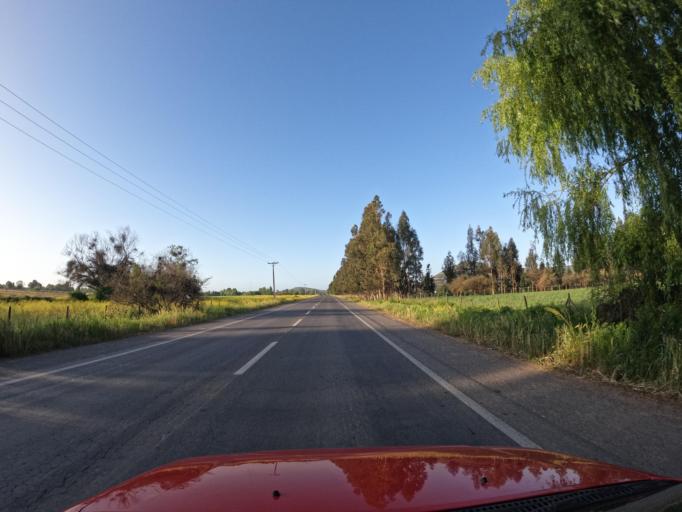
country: CL
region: O'Higgins
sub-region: Provincia de Colchagua
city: Santa Cruz
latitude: -34.3663
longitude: -71.4145
